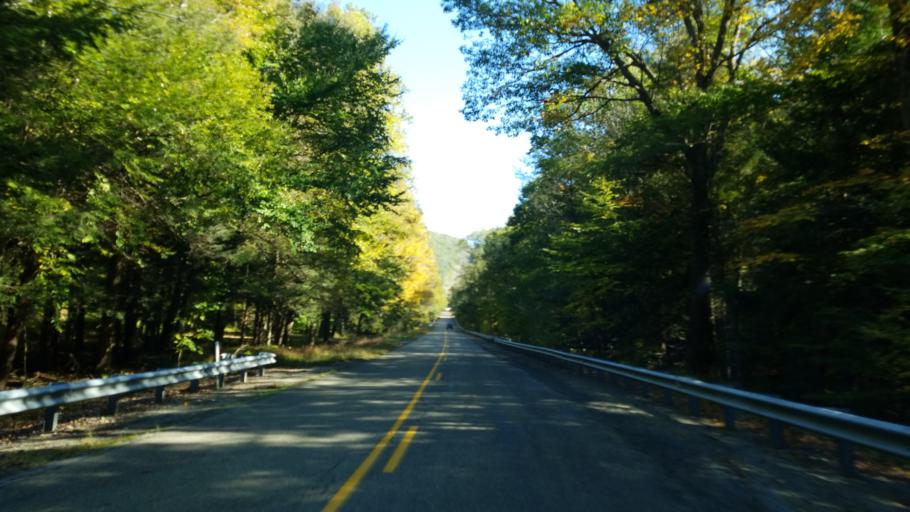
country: US
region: Pennsylvania
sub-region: Elk County
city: Saint Marys
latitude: 41.2665
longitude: -78.4018
